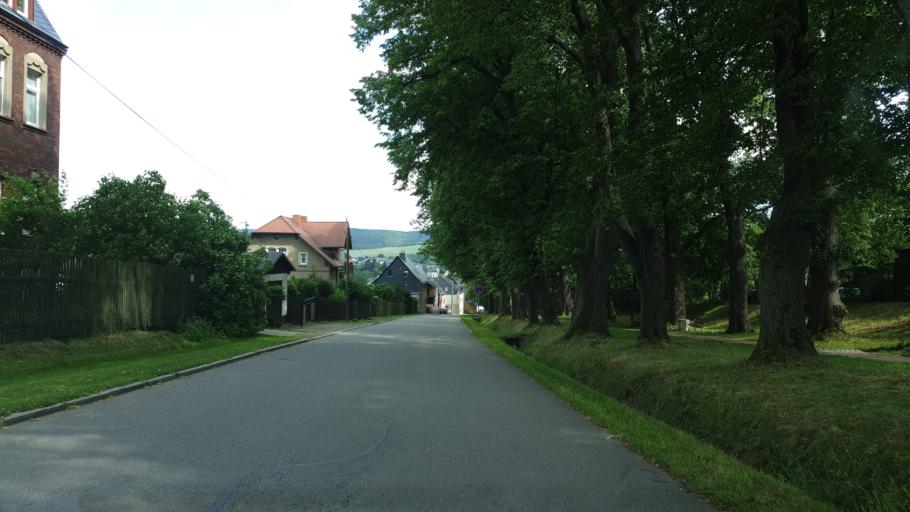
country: DE
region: Saxony
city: Lossnitz
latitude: 50.6258
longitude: 12.7283
